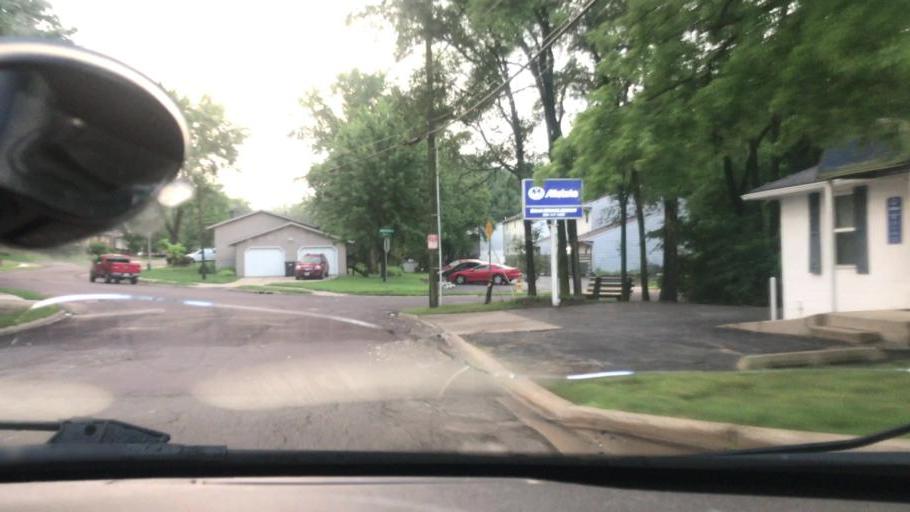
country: US
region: Illinois
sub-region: Tazewell County
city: Pekin
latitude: 40.5582
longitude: -89.6169
